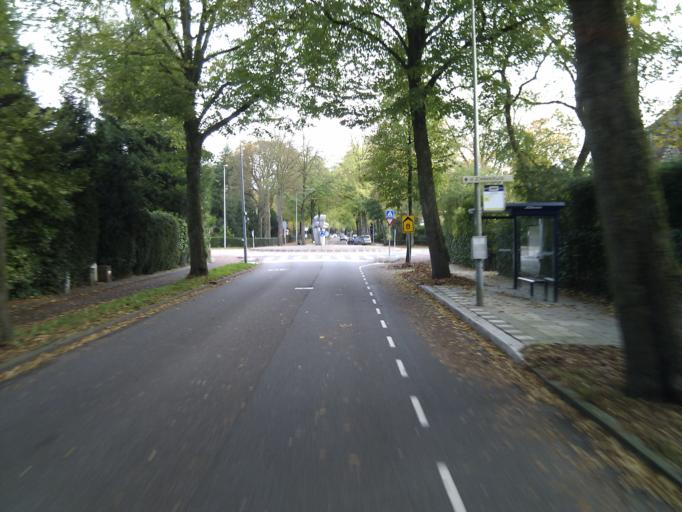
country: NL
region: Utrecht
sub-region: Gemeente Zeist
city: Zeist
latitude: 52.0936
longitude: 5.2543
